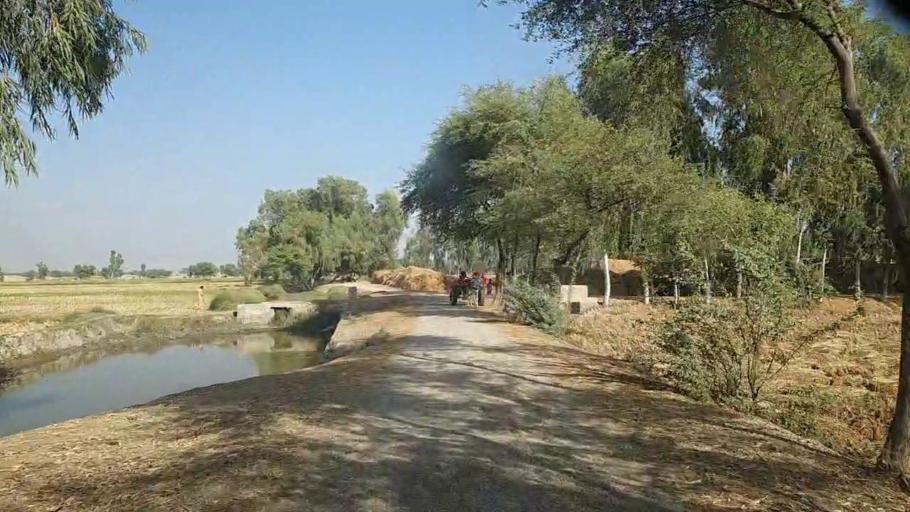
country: PK
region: Sindh
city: Tangwani
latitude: 28.2853
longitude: 69.0002
